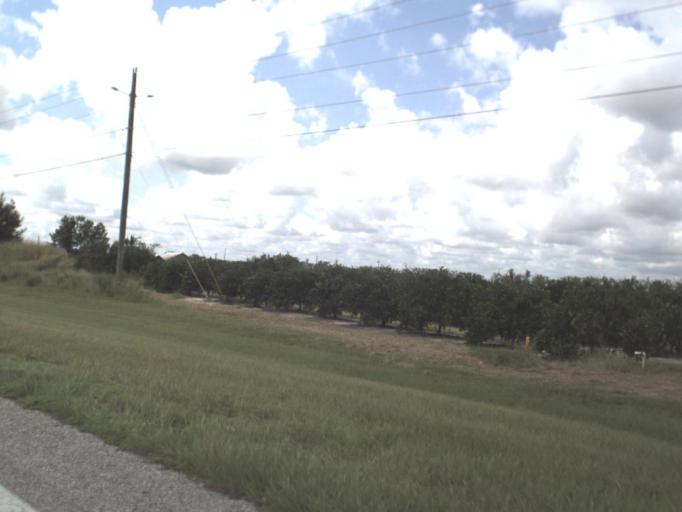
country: US
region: Florida
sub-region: Hardee County
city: Zolfo Springs
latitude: 27.5186
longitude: -81.8092
